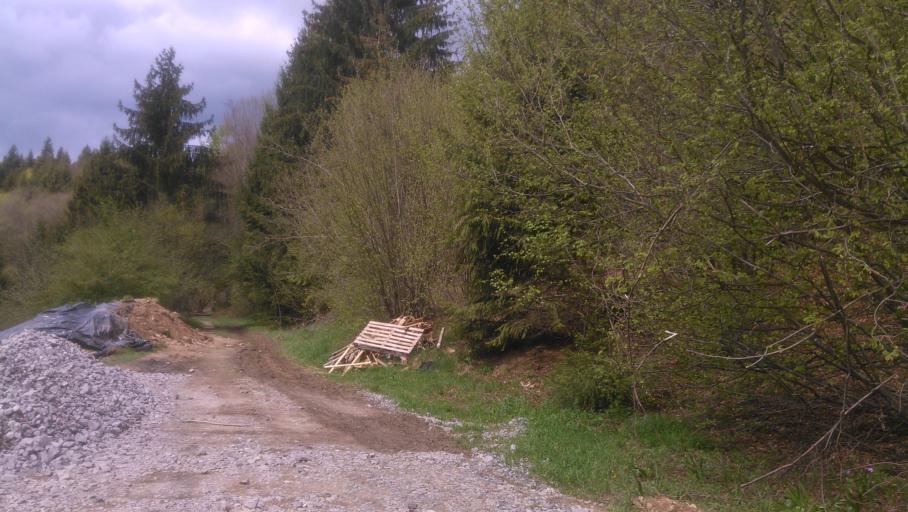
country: SK
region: Banskobystricky
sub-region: Okres Banska Bystrica
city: Brezno
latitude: 48.8768
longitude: 19.5822
